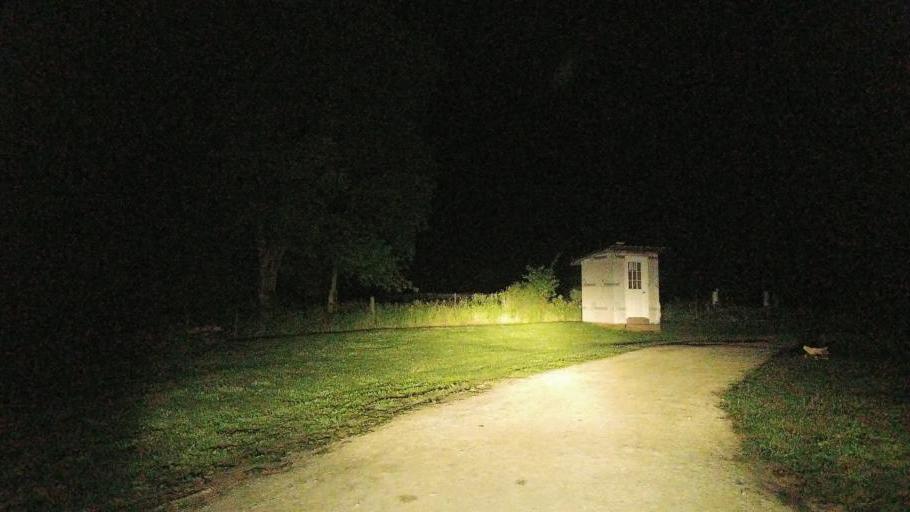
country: US
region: Iowa
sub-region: Decatur County
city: Lamoni
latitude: 40.6387
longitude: -94.0330
